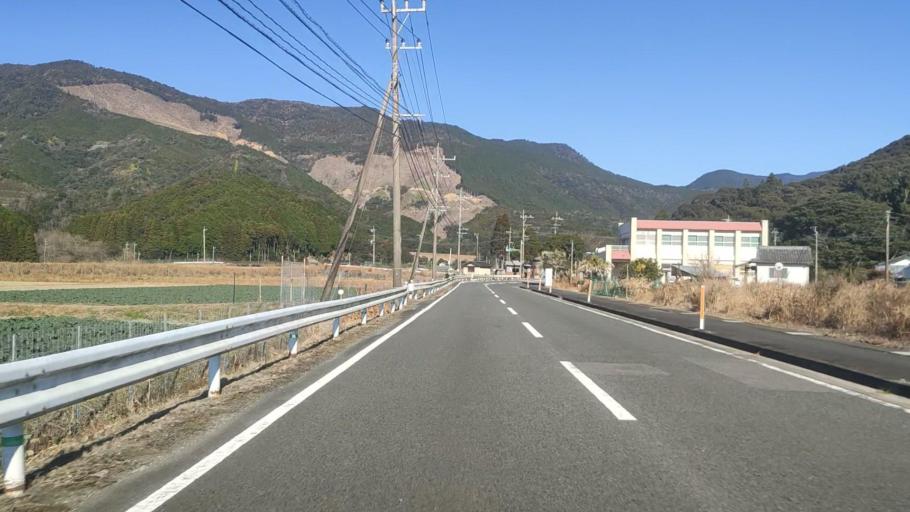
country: JP
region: Miyazaki
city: Nobeoka
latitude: 32.6828
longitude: 131.7873
